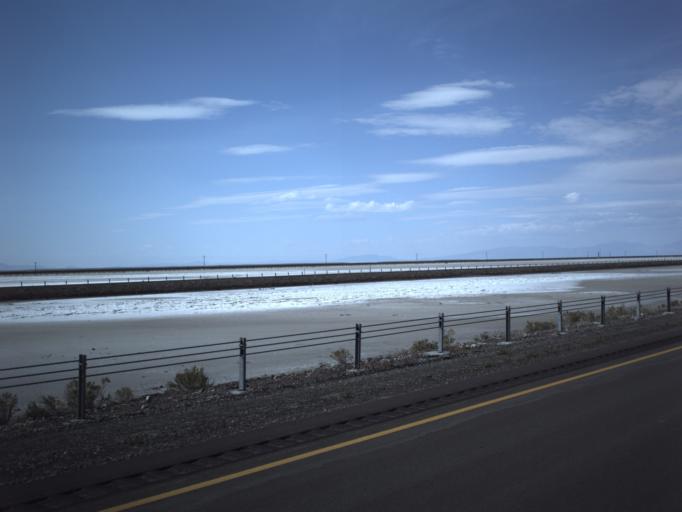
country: US
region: Utah
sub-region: Tooele County
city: Wendover
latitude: 40.7300
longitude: -113.4211
